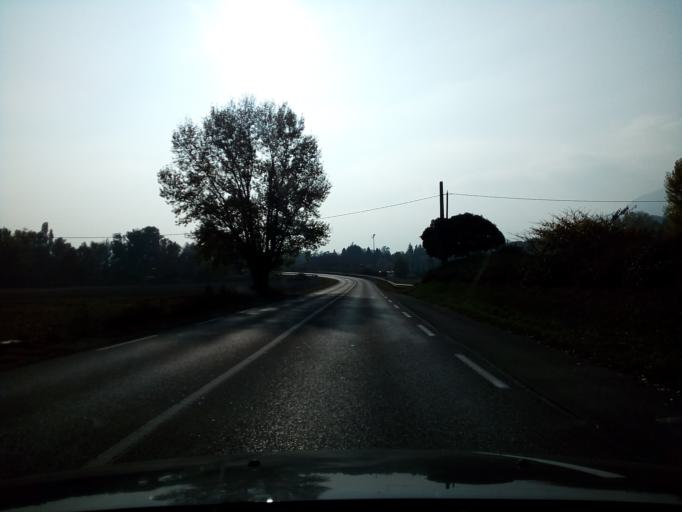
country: FR
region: Rhone-Alpes
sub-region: Departement de l'Isere
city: Montbonnot-Saint-Martin
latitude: 45.2273
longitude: 5.8230
